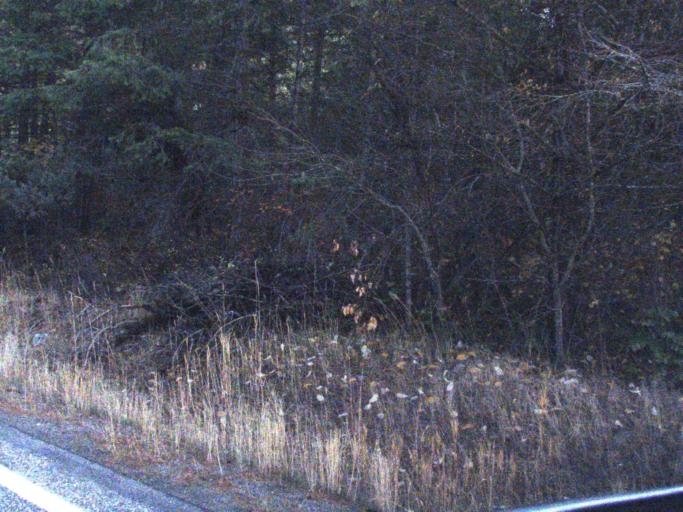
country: US
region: Washington
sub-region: Stevens County
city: Kettle Falls
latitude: 48.8140
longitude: -117.9315
